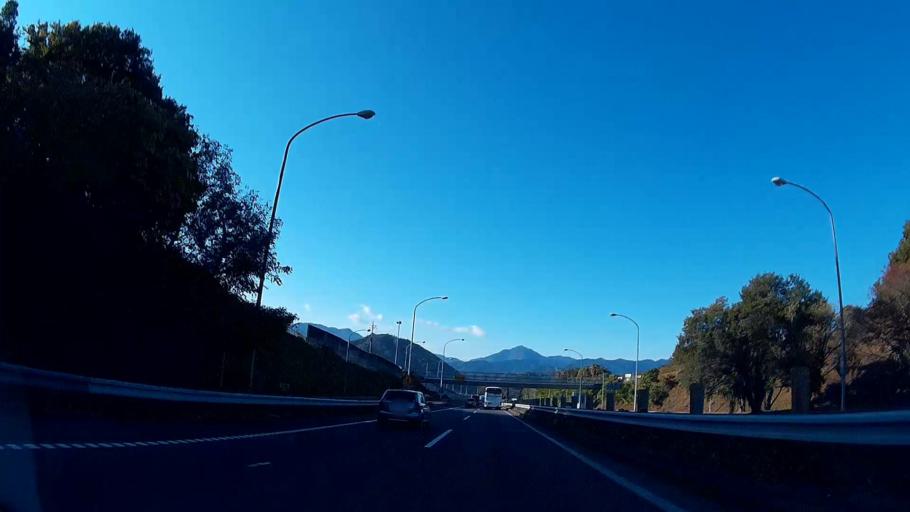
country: JP
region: Yamanashi
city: Uenohara
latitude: 35.6206
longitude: 139.1667
